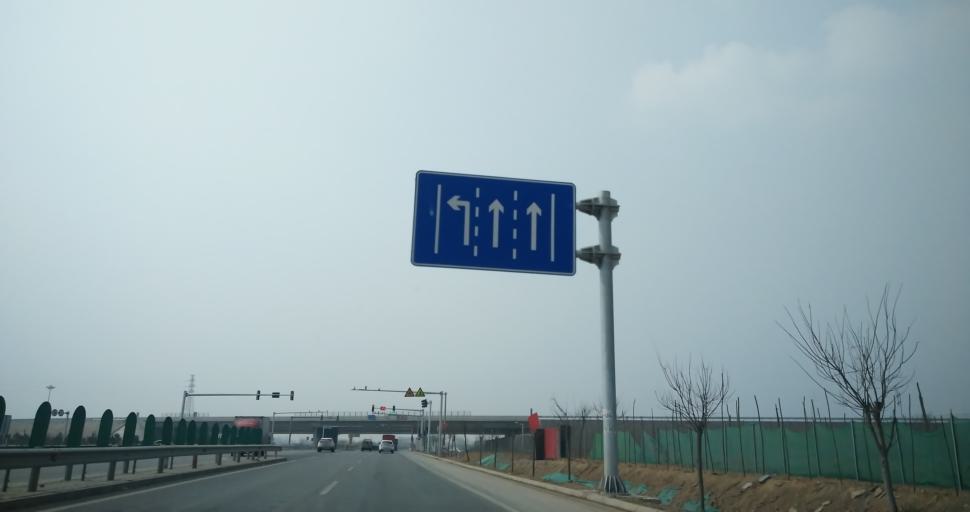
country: CN
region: Beijing
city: Qingyundian
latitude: 39.6845
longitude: 116.4525
